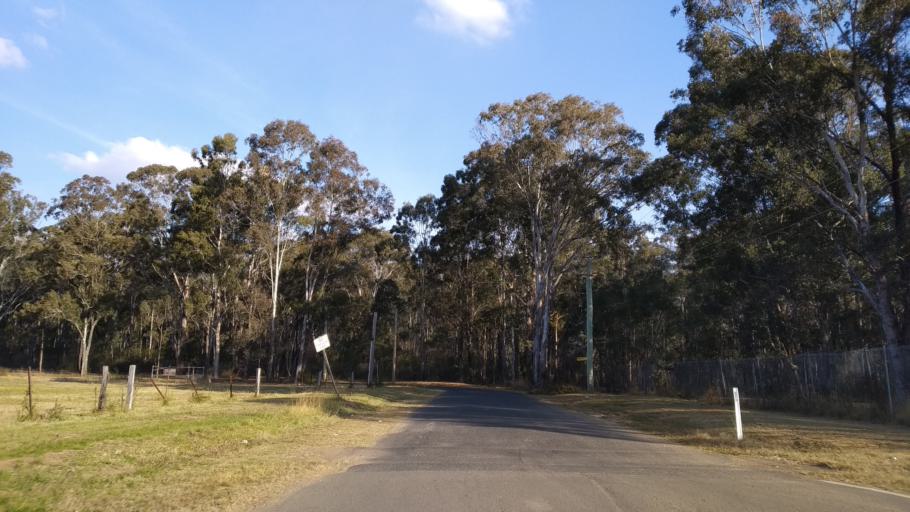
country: AU
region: New South Wales
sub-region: Penrith Municipality
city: Werrington County
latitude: -33.7163
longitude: 150.7554
